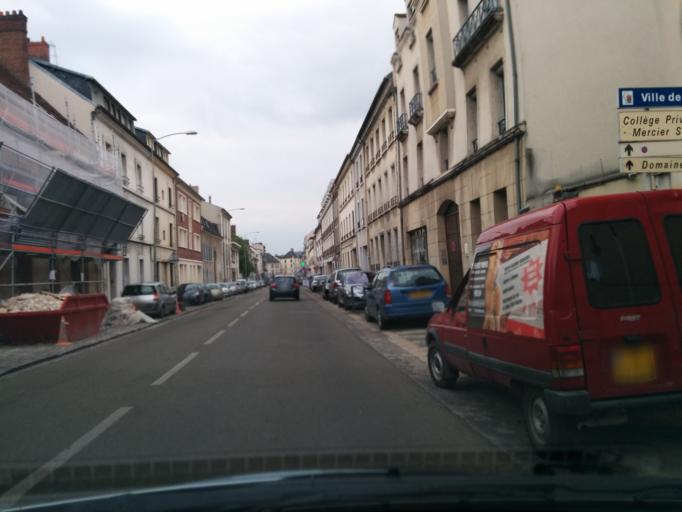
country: FR
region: Ile-de-France
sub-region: Departement des Yvelines
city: Meulan-en-Yvelines
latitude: 49.0055
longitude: 1.9138
